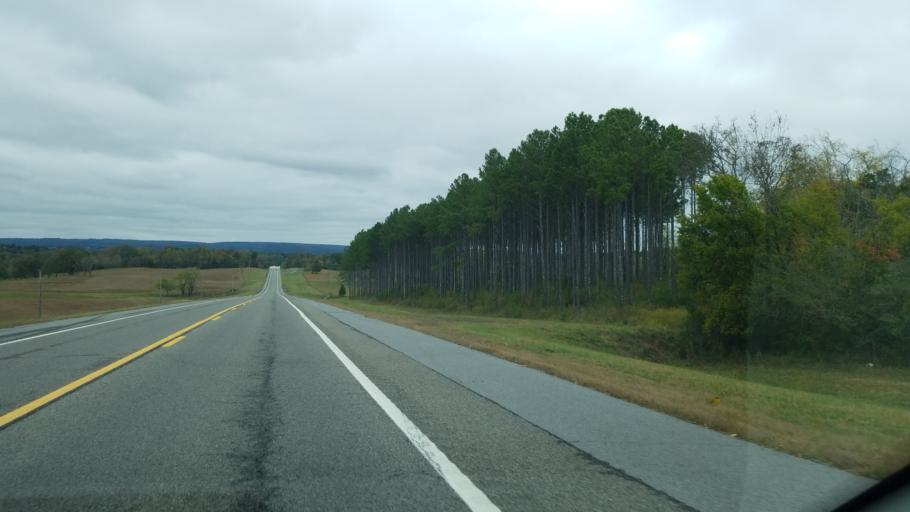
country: US
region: Tennessee
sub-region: Rhea County
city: Graysville
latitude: 35.3977
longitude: -85.0114
